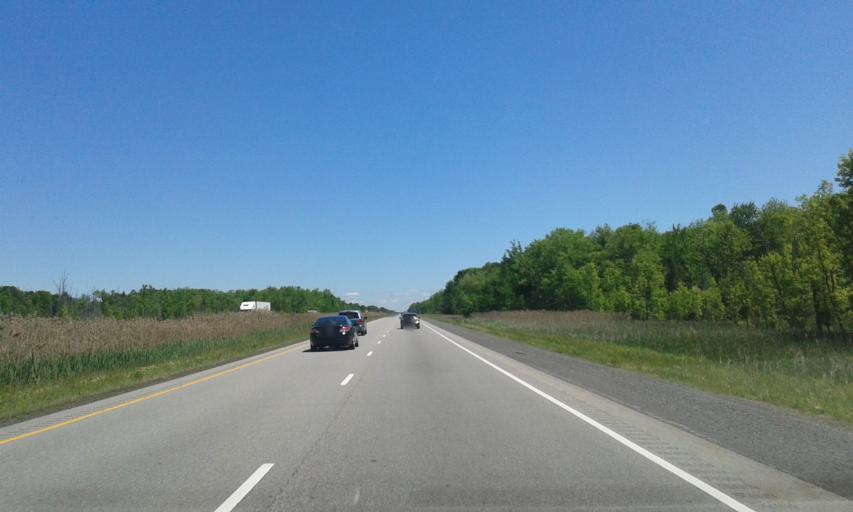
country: CA
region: Ontario
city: Prescott
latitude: 44.7889
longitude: -75.4397
